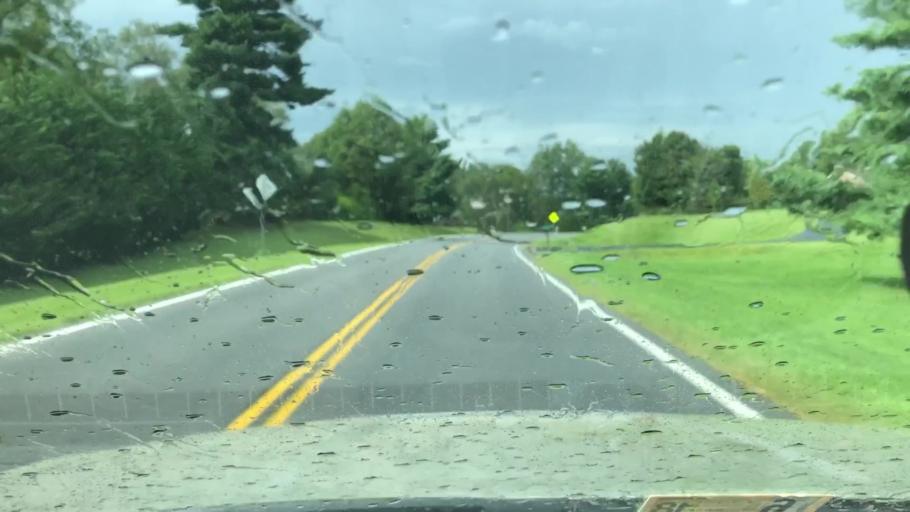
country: US
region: Virginia
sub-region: City of Waynesboro
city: Waynesboro
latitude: 38.0867
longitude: -78.9015
